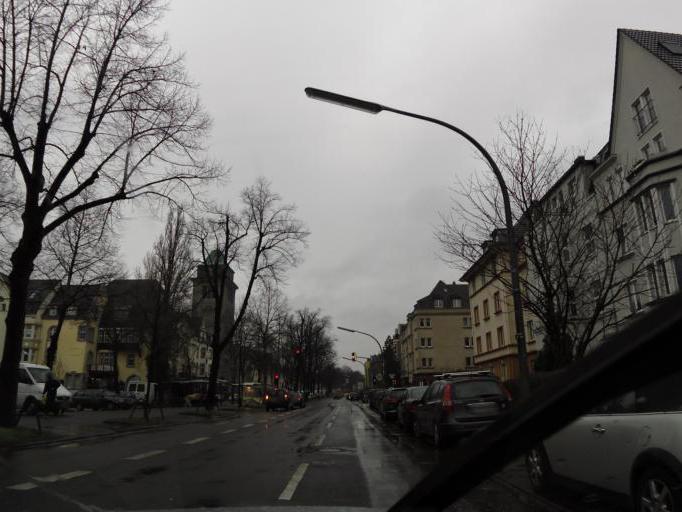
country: DE
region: North Rhine-Westphalia
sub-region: Regierungsbezirk Koln
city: Neustadt/Sued
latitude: 50.9109
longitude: 6.9270
